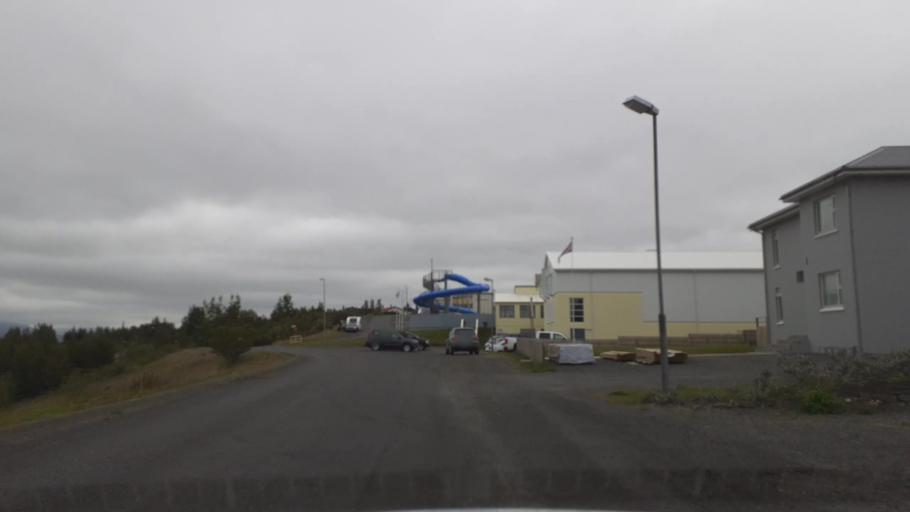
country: IS
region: Northwest
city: Saudarkrokur
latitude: 65.5542
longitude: -19.4510
